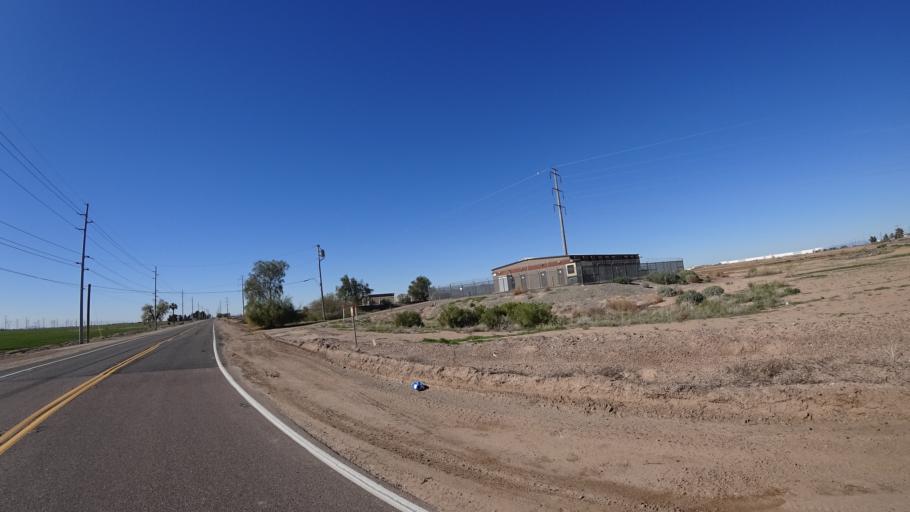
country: US
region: Arizona
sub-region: Maricopa County
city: Goodyear
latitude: 33.4065
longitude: -112.3578
